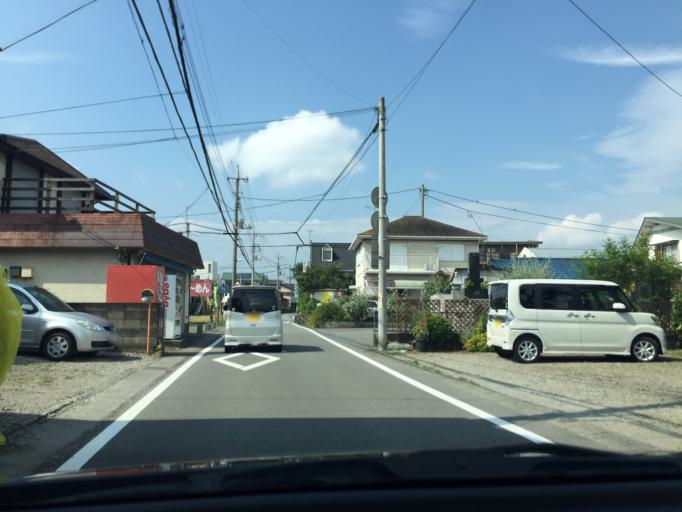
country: JP
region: Shizuoka
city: Mishima
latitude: 35.1398
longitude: 138.8999
